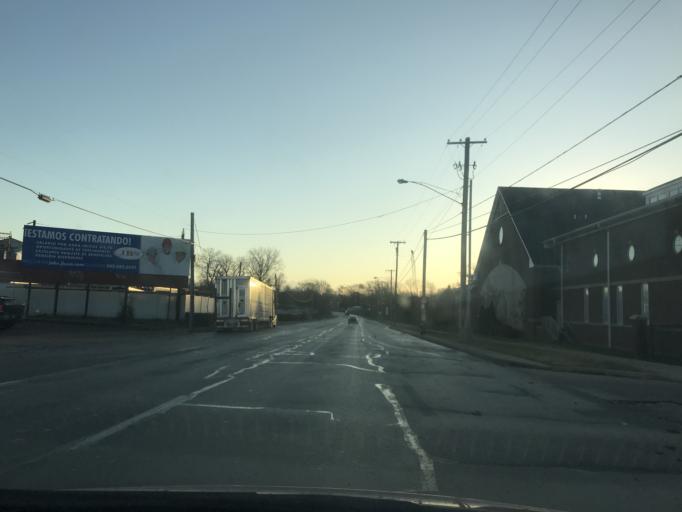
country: US
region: Indiana
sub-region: Clark County
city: Jeffersonville
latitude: 38.2537
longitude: -85.7302
